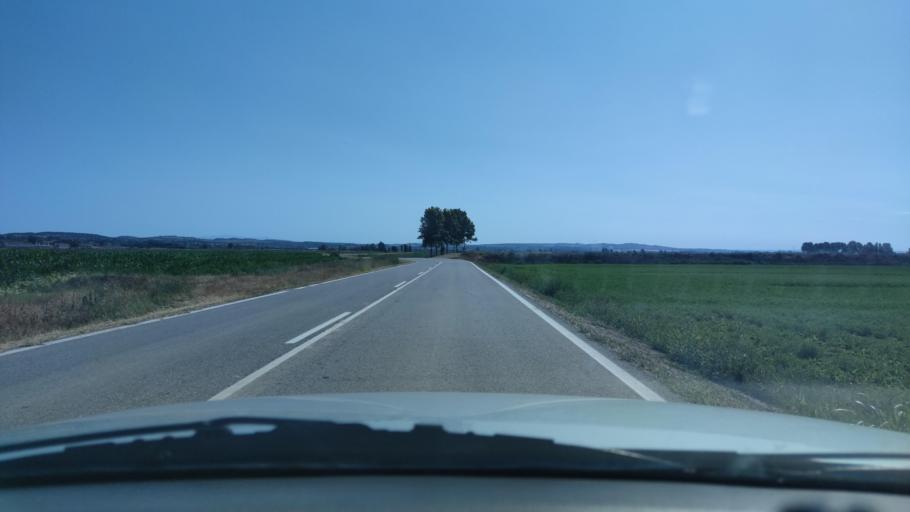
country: ES
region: Catalonia
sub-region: Provincia de Lleida
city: Bellcaire d'Urgell
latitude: 41.7335
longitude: 0.9346
